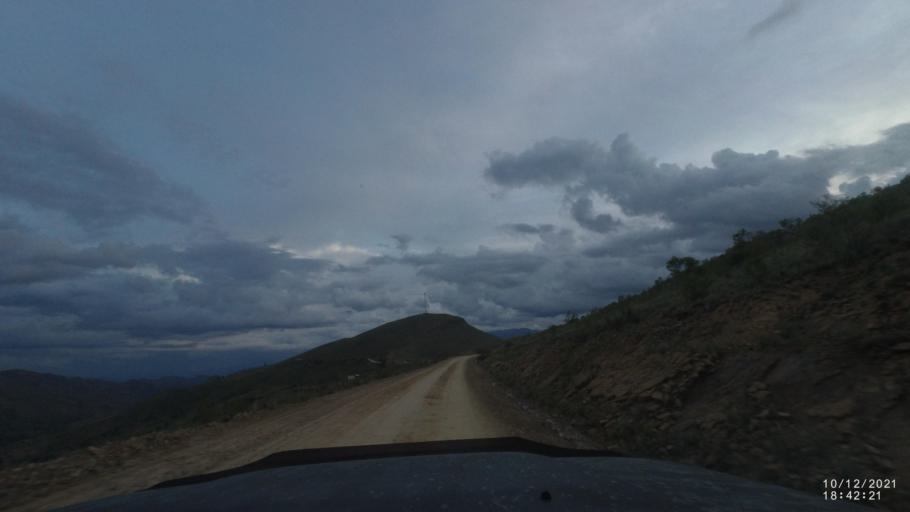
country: BO
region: Cochabamba
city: Tarata
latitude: -17.8688
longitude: -65.9843
